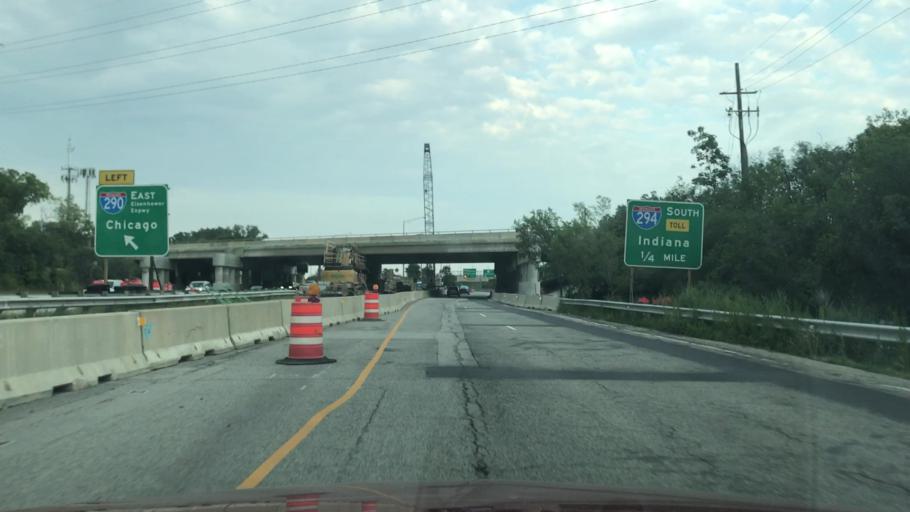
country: US
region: Illinois
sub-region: Cook County
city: Hillside
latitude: 41.8617
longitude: -87.9267
